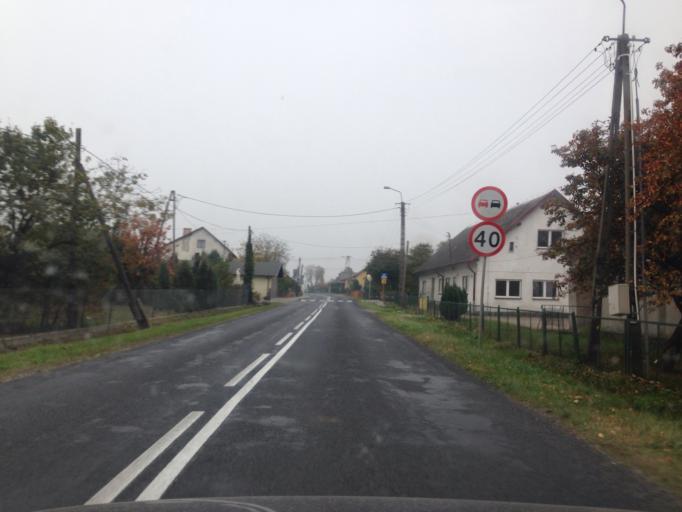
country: PL
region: Kujawsko-Pomorskie
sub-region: Powiat brodnicki
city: Bartniczka
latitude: 53.2495
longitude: 19.5661
